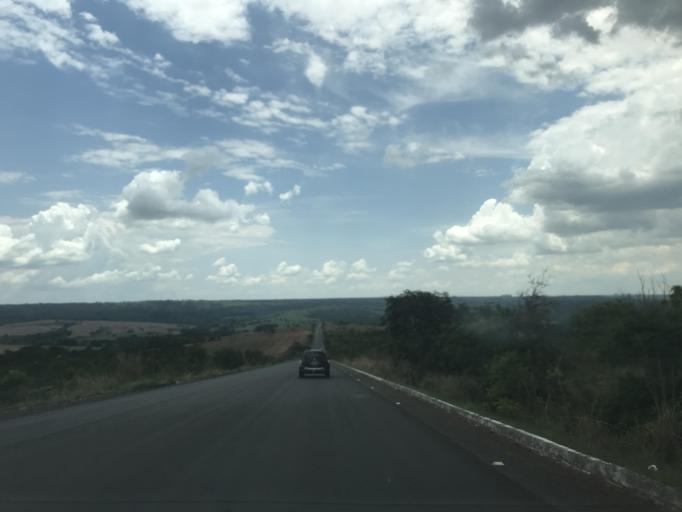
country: BR
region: Goias
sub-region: Vianopolis
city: Vianopolis
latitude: -16.9438
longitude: -48.5593
